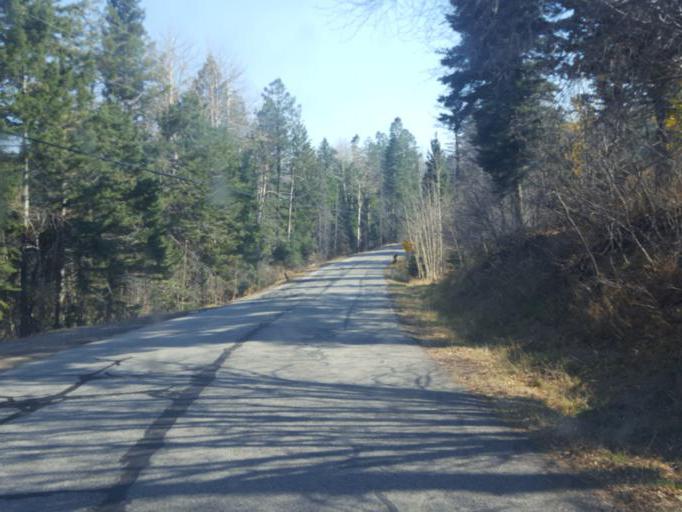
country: US
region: New Mexico
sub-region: Los Alamos County
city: Los Alamos
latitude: 35.8934
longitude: -106.3854
